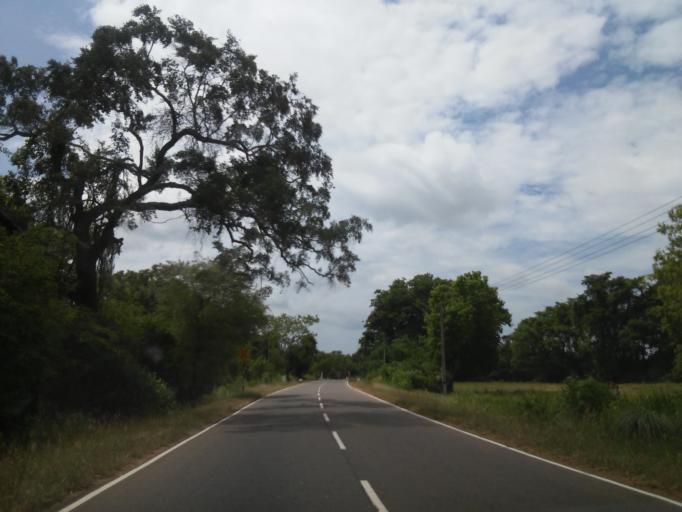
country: LK
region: Central
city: Sigiriya
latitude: 8.0772
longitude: 80.6790
